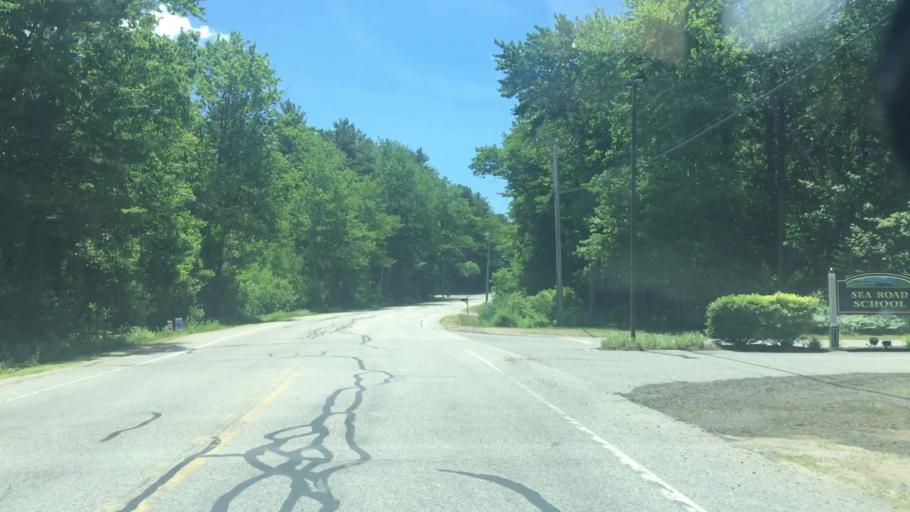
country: US
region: Maine
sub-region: York County
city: Kennebunk
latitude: 43.3776
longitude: -70.5279
